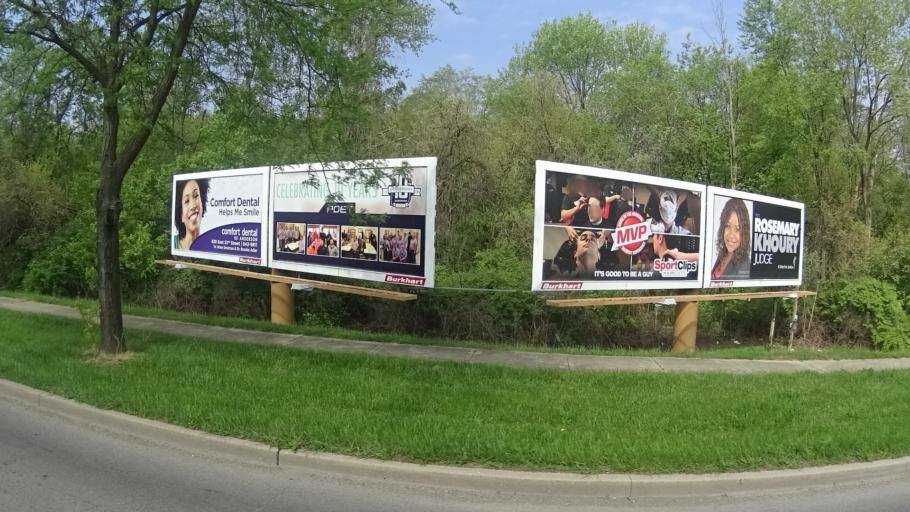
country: US
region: Indiana
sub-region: Madison County
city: Anderson
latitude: 40.1288
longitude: -85.6781
